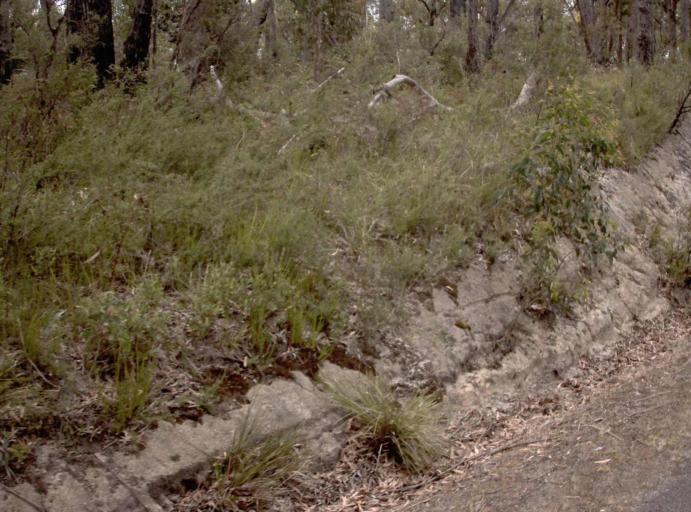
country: AU
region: New South Wales
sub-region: Bega Valley
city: Eden
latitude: -37.4929
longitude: 149.5502
